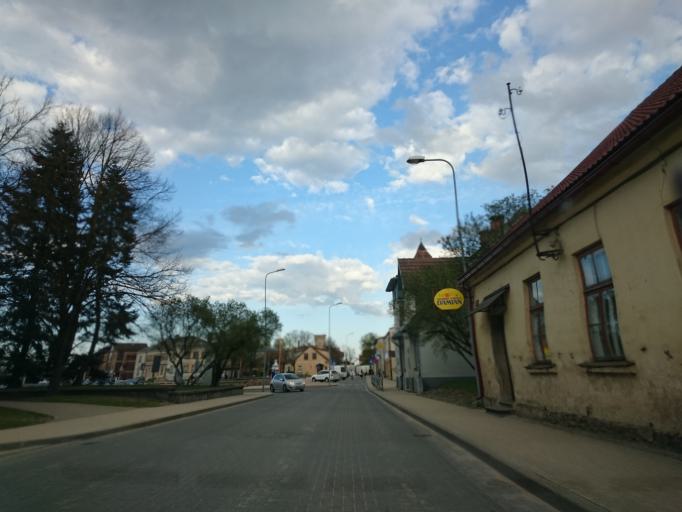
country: LV
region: Kuldigas Rajons
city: Kuldiga
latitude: 56.9685
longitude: 21.9593
